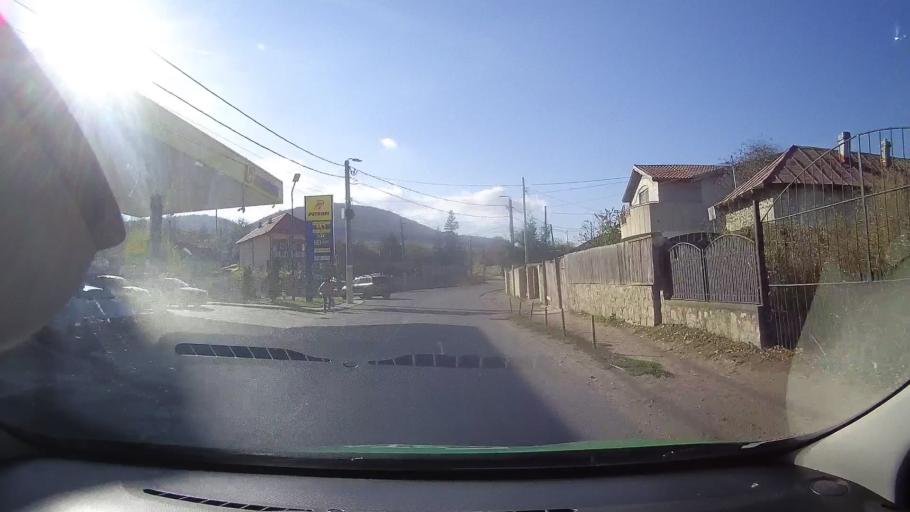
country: RO
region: Tulcea
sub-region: Oras Babadag
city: Babadag
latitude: 44.8917
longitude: 28.7167
